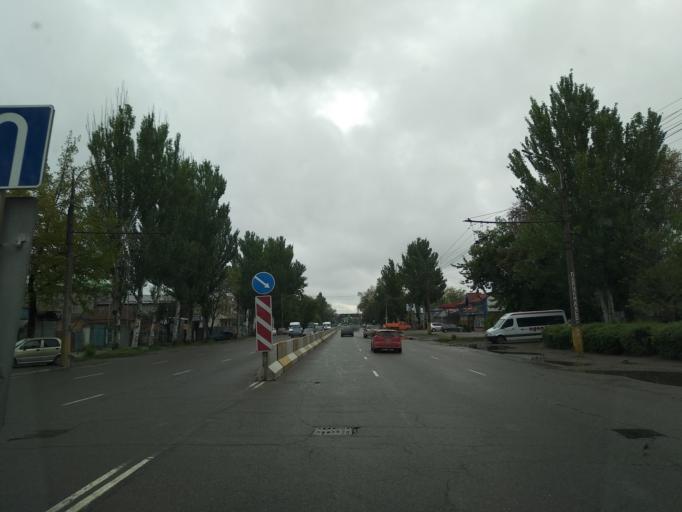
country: KG
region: Chuy
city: Lebedinovka
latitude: 42.8886
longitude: 74.6510
